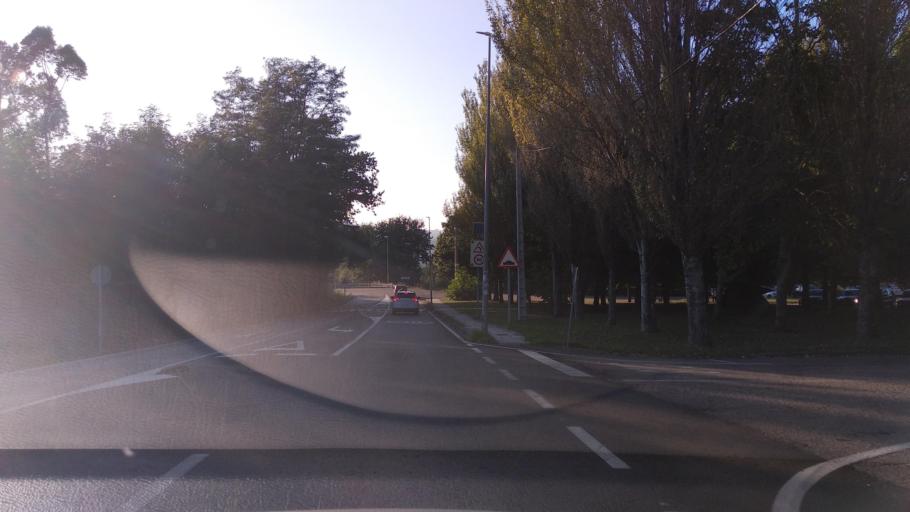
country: ES
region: Galicia
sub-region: Provincia de Pontevedra
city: Redondela
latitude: 42.3408
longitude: -8.5925
